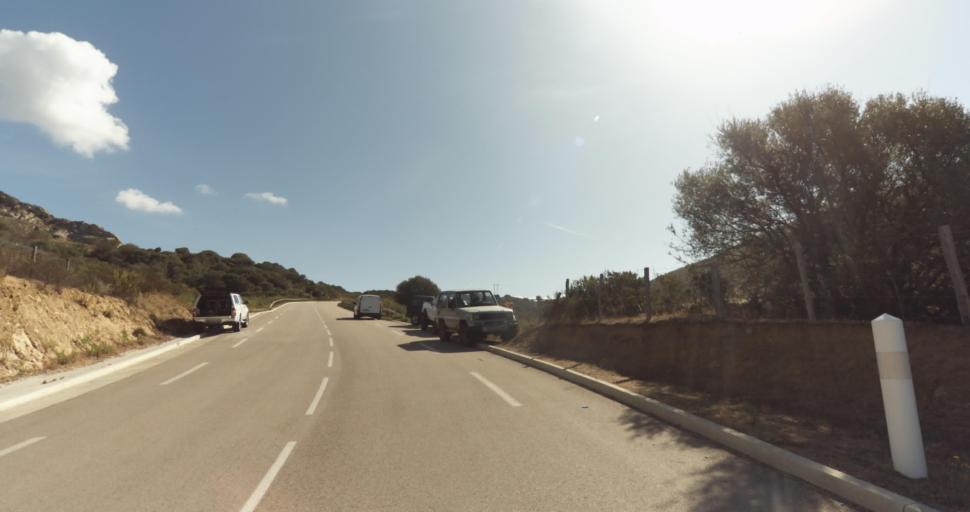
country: FR
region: Corsica
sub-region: Departement de la Corse-du-Sud
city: Ajaccio
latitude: 41.9325
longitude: 8.6725
